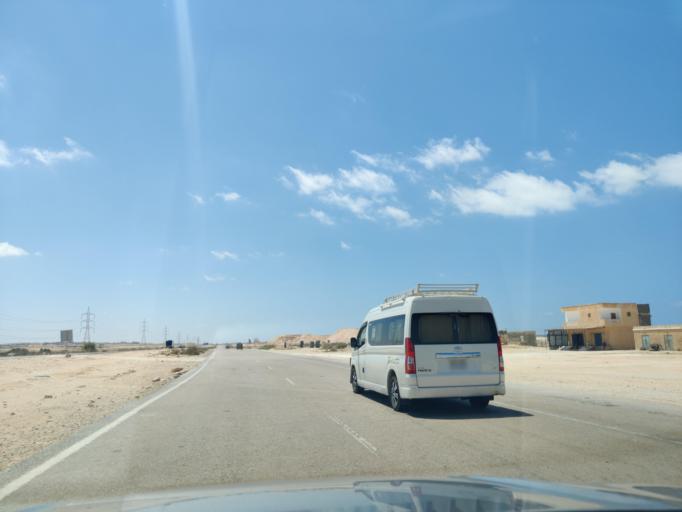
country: EG
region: Muhafazat Matruh
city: Al `Alamayn
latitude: 31.0641
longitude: 28.1969
